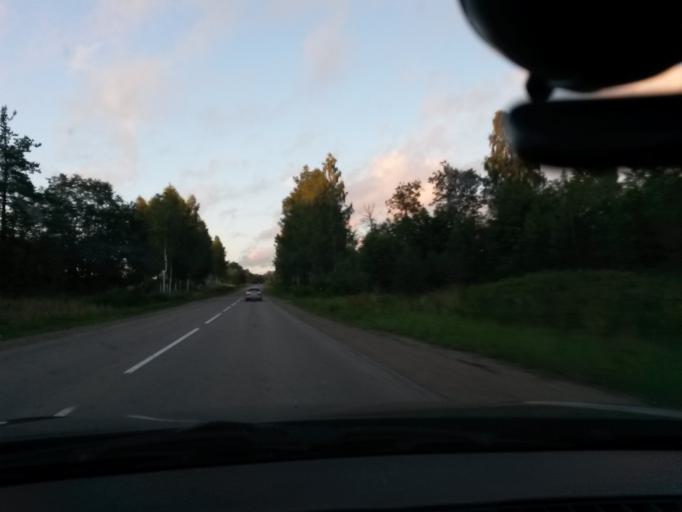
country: LV
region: Madonas Rajons
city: Madona
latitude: 56.7993
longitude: 26.0342
